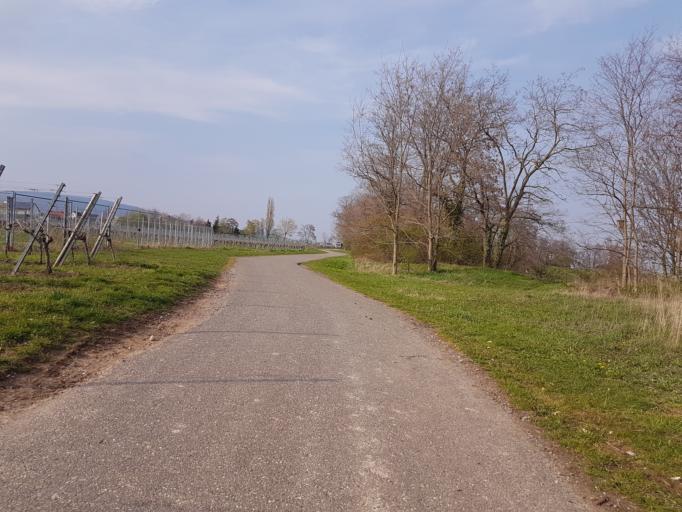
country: DE
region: Rheinland-Pfalz
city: Edesheim
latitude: 49.2755
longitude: 8.1382
